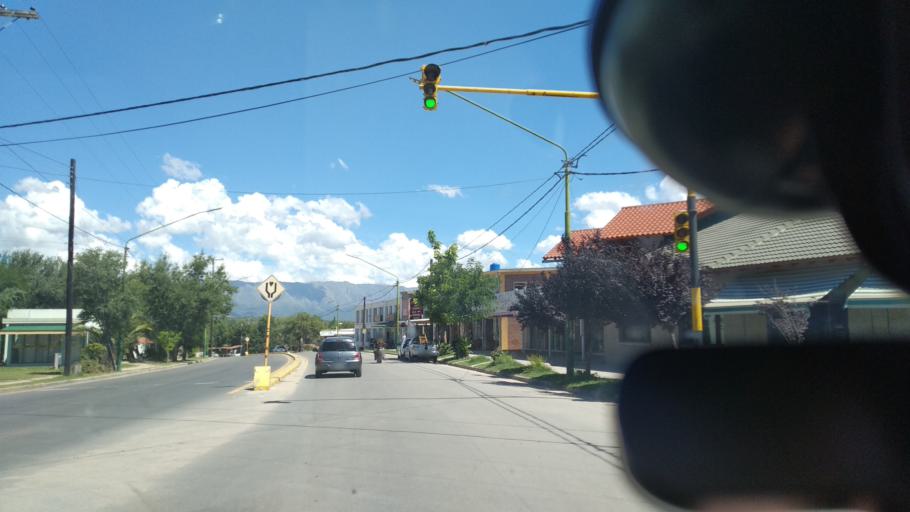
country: AR
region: Cordoba
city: Mina Clavero
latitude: -31.7176
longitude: -65.0117
